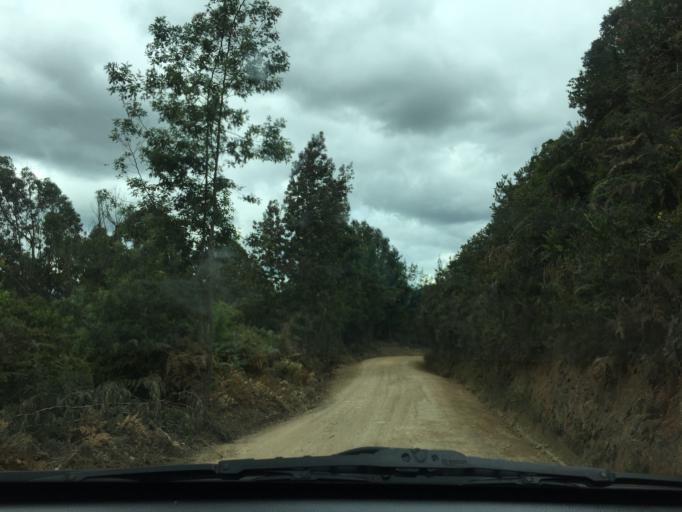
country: CO
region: Cundinamarca
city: Tabio
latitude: 4.9223
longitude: -74.1082
